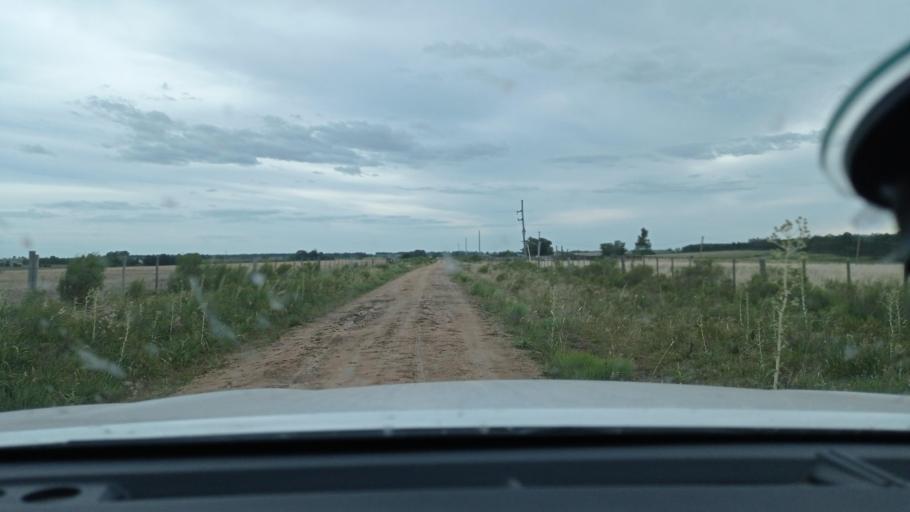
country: UY
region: Florida
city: Casupa
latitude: -34.1365
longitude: -55.8021
